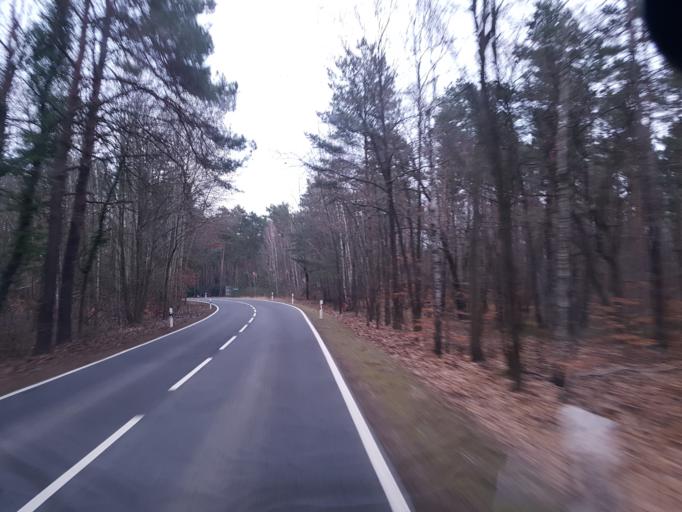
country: DE
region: Brandenburg
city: Sallgast
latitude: 51.5811
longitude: 13.8395
